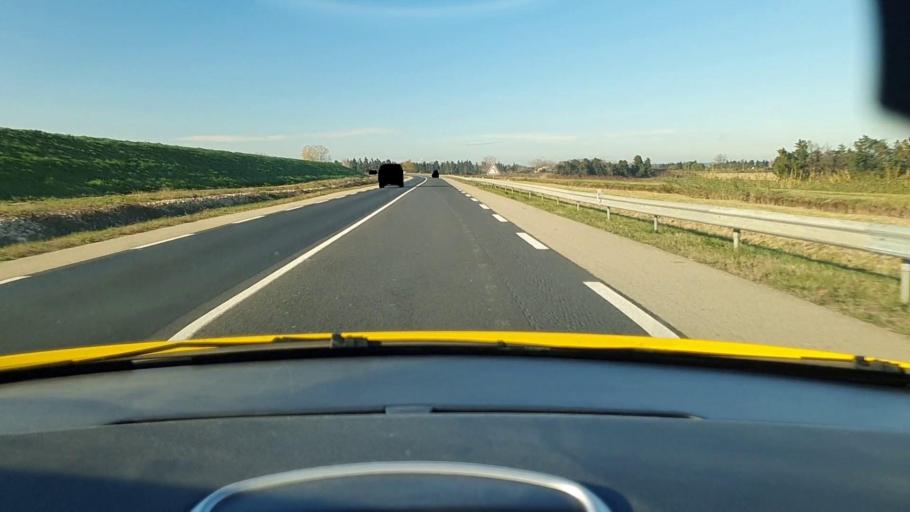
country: FR
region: Languedoc-Roussillon
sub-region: Departement du Gard
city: Fourques
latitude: 43.6965
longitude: 4.5868
